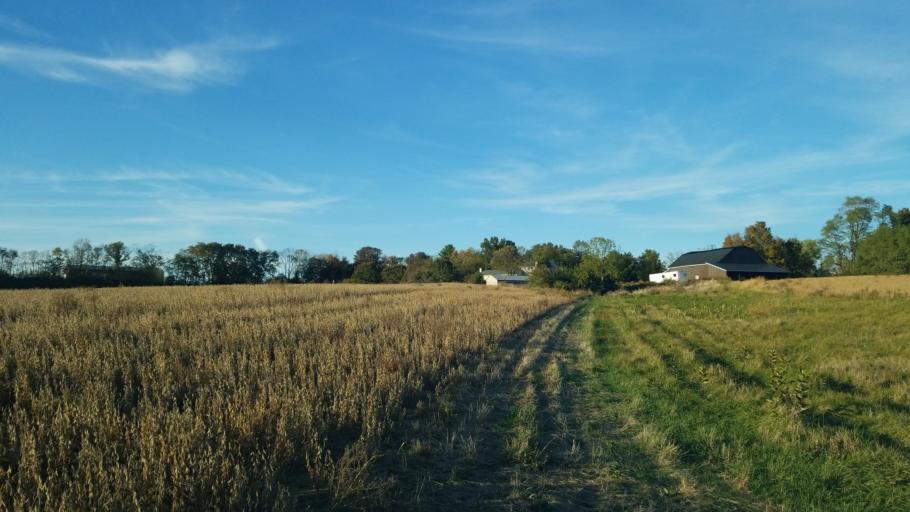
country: US
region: Ohio
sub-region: Warren County
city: Morrow
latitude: 39.4033
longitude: -84.0764
